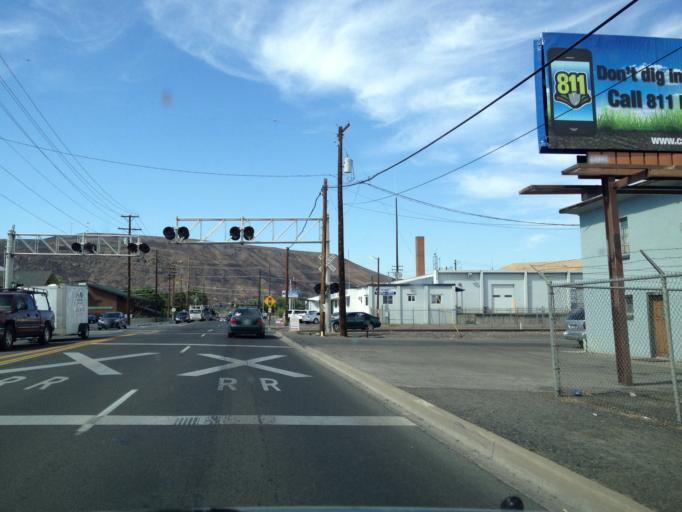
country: US
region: Washington
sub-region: Yakima County
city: Yakima
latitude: 46.6155
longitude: -120.5303
